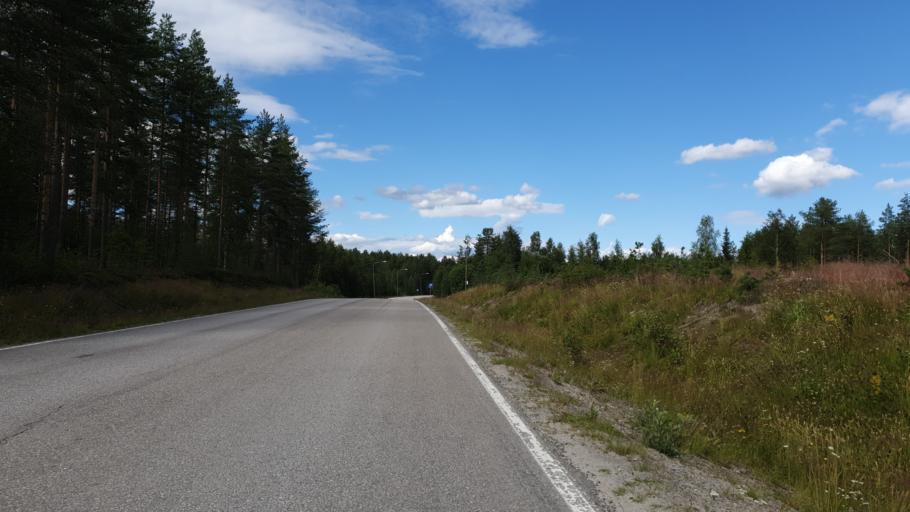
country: FI
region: Kainuu
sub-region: Kehys-Kainuu
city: Kuhmo
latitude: 64.1149
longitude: 29.5275
